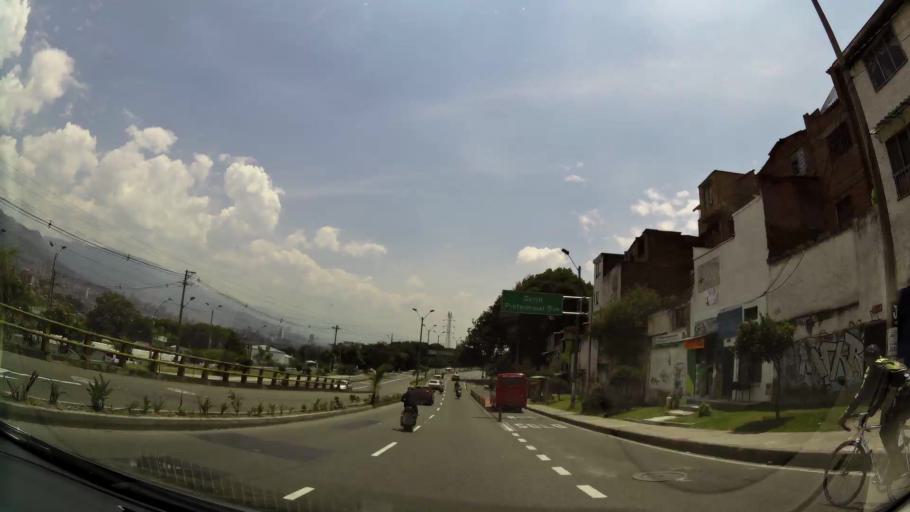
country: CO
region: Antioquia
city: Medellin
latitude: 6.2866
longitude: -75.5705
